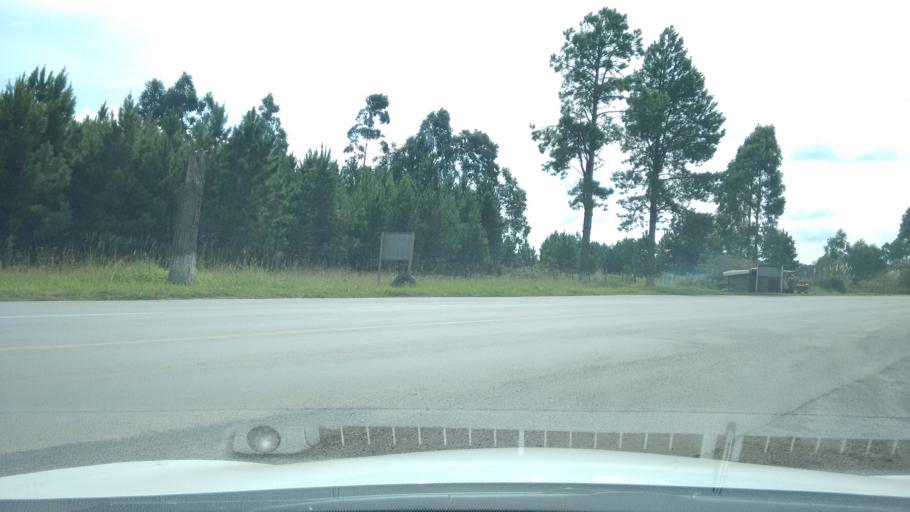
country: BR
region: Santa Catarina
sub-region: Curitibanos
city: Curitibanos
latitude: -27.3014
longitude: -50.4222
